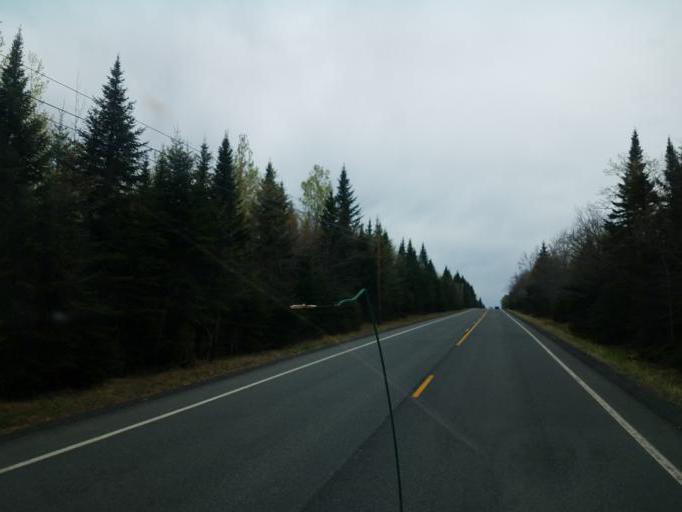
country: US
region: Maine
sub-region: Penobscot County
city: Patten
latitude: 46.2953
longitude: -68.3574
